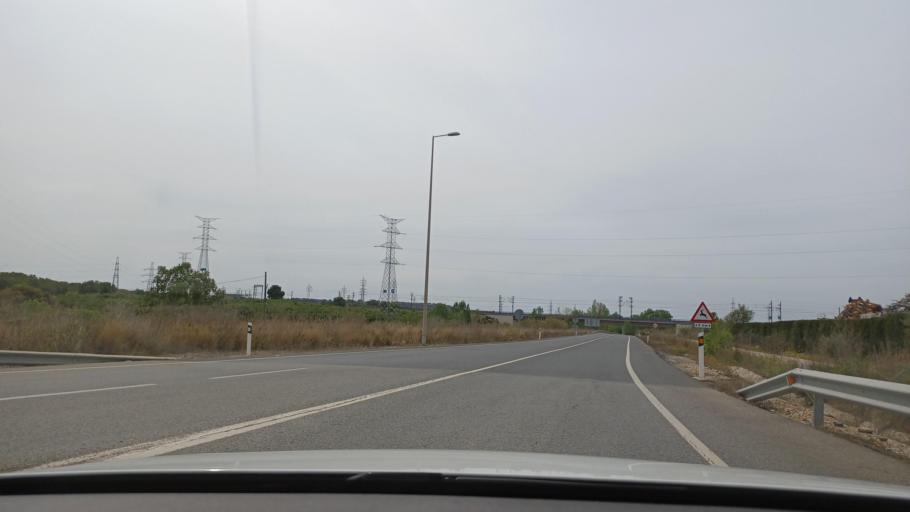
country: ES
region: Catalonia
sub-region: Provincia de Tarragona
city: la Pobla de Mafumet
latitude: 41.2011
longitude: 1.2432
